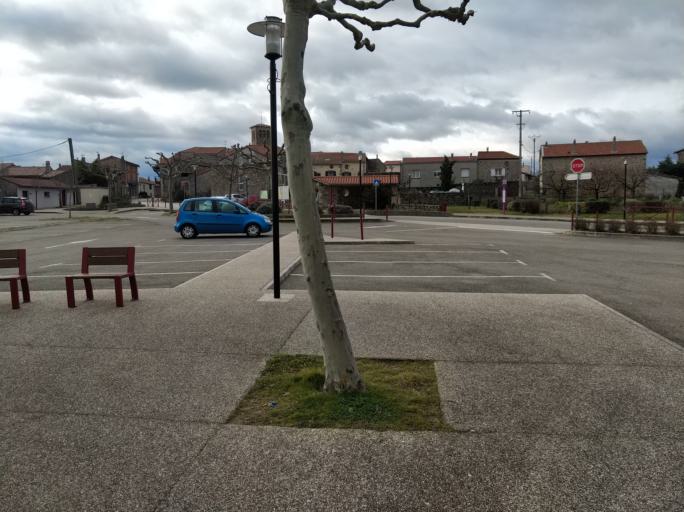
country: FR
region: Rhone-Alpes
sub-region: Departement de l'Ardeche
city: Vernosc-les-Annonay
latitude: 45.1881
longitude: 4.7367
